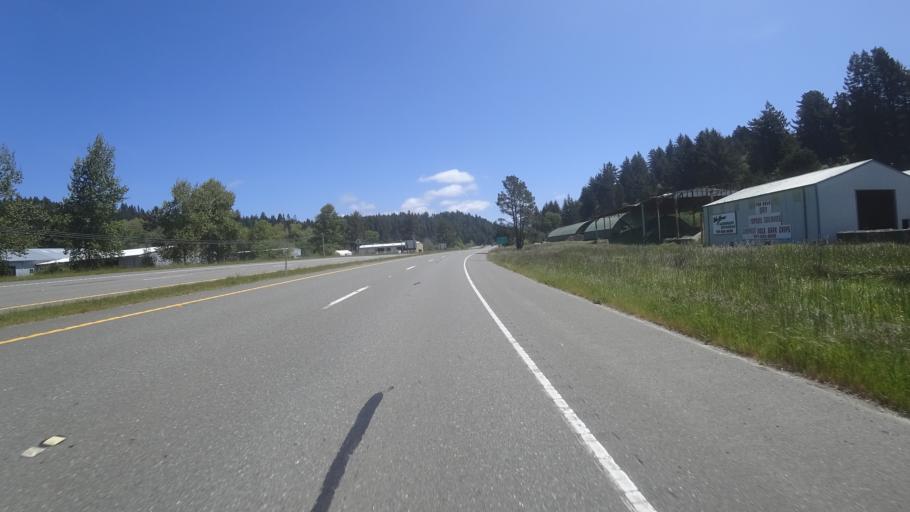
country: US
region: California
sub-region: Humboldt County
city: Arcata
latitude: 40.9103
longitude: -124.0681
